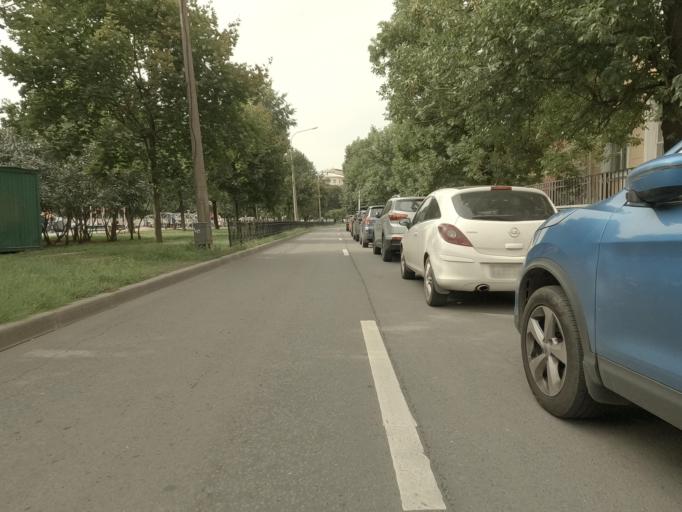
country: RU
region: St.-Petersburg
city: Admiralteisky
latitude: 59.9124
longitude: 30.2858
